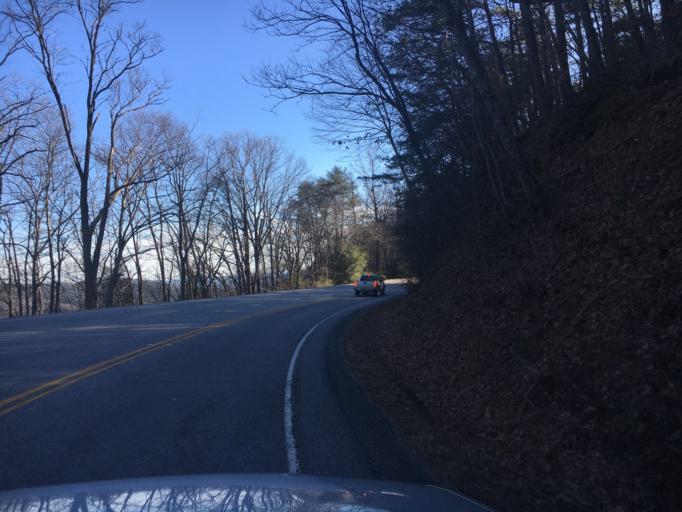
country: US
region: Georgia
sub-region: Union County
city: Blairsville
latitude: 34.7328
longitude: -83.9213
